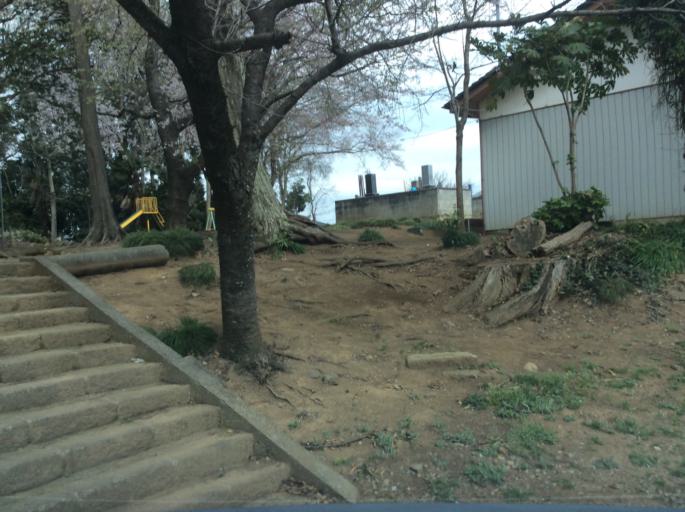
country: JP
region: Ibaraki
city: Ishige
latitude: 36.1758
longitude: 139.9495
